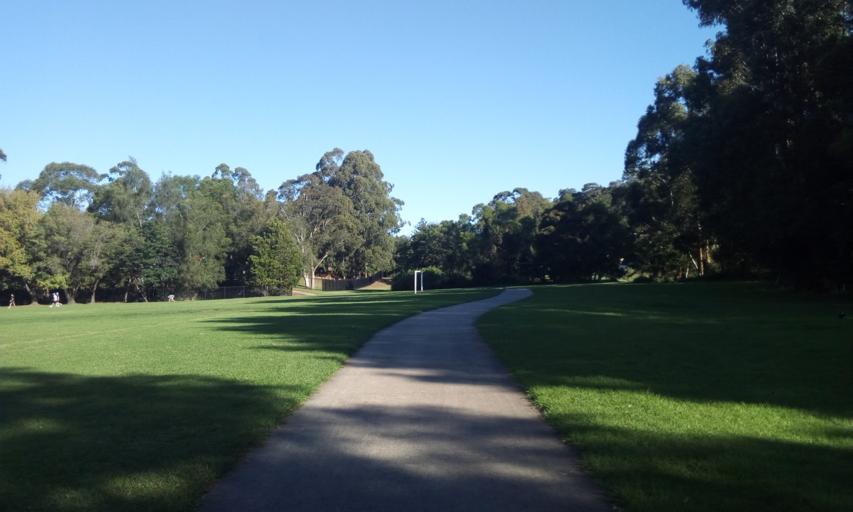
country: AU
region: New South Wales
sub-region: Wollongong
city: West Wollongong
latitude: -34.4282
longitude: 150.8602
